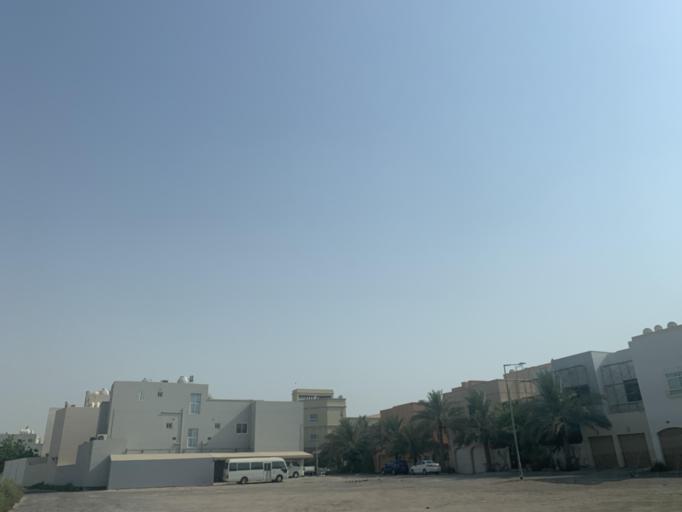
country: BH
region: Manama
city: Jidd Hafs
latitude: 26.2089
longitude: 50.4935
